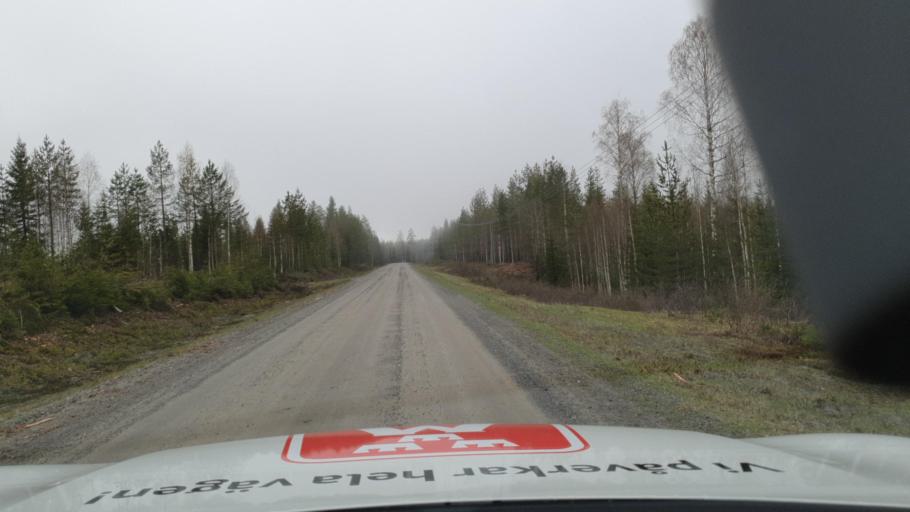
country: SE
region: Vaesterbotten
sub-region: Nordmalings Kommun
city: Nordmaling
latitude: 63.7630
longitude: 19.4811
